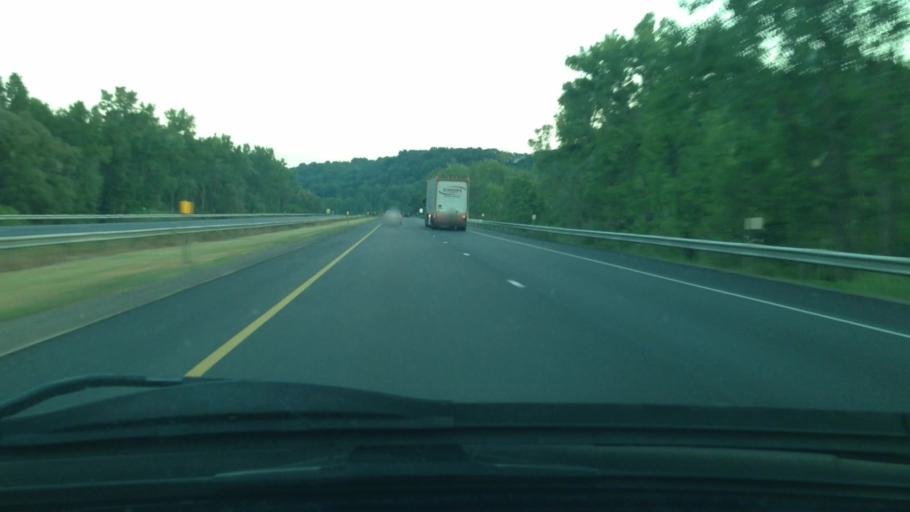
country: US
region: New York
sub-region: Montgomery County
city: Fort Plain
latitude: 42.9243
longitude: -74.6140
